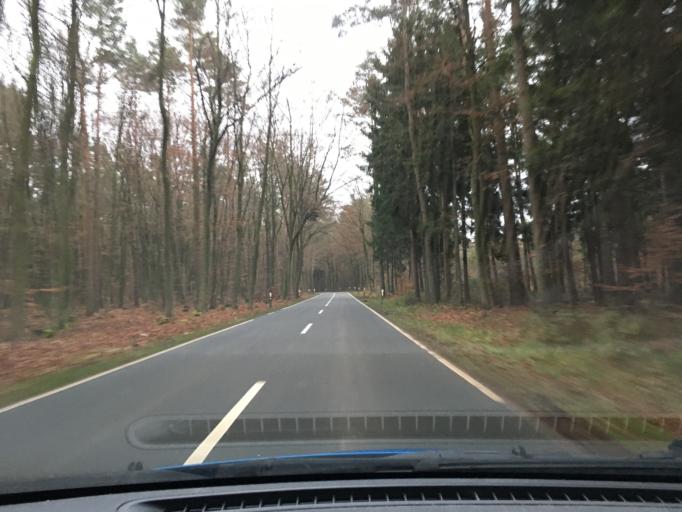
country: DE
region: Lower Saxony
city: Tosterglope
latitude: 53.2567
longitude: 10.8078
